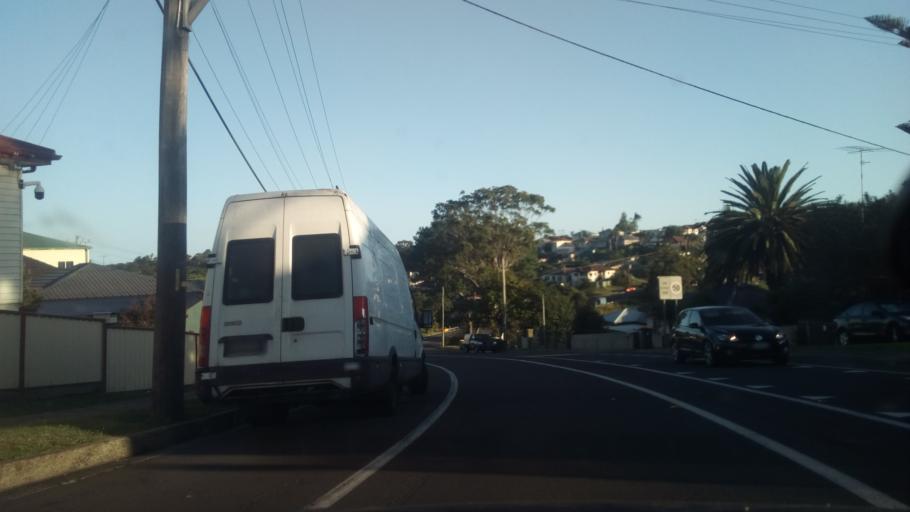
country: AU
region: New South Wales
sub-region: Wollongong
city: Lake Heights
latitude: -34.4734
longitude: 150.8712
